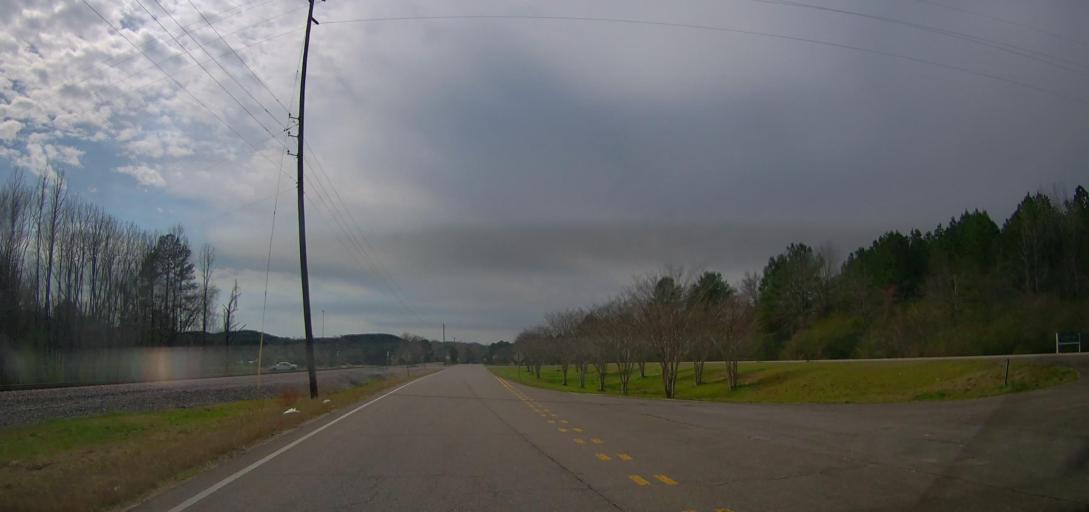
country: US
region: Alabama
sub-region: Walker County
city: Carbon Hill
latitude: 33.8771
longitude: -87.4935
